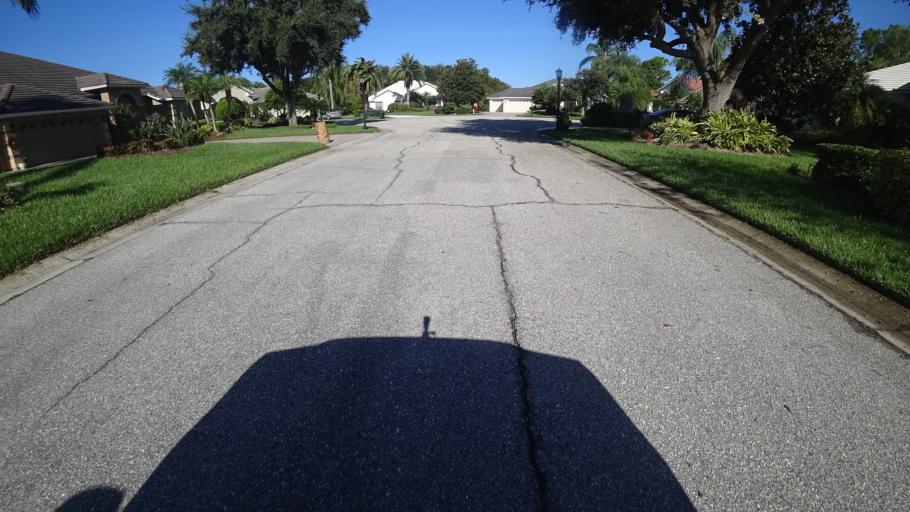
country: US
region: Florida
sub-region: Sarasota County
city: Desoto Lakes
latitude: 27.4341
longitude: -82.4715
